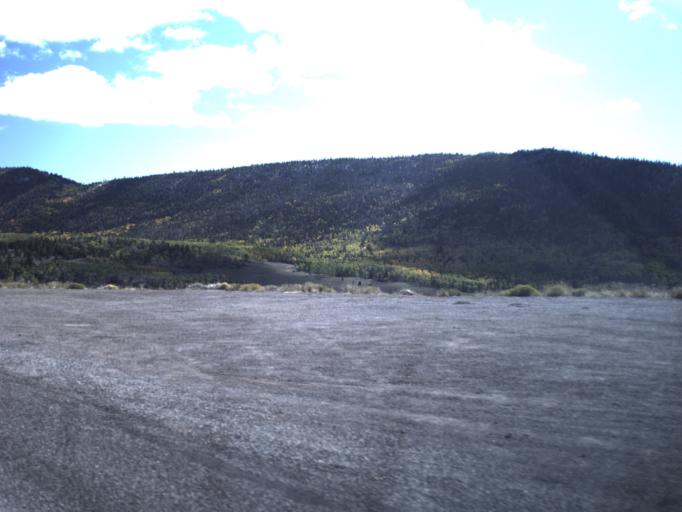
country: US
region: Utah
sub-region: Wayne County
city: Loa
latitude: 38.5159
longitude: -111.7593
